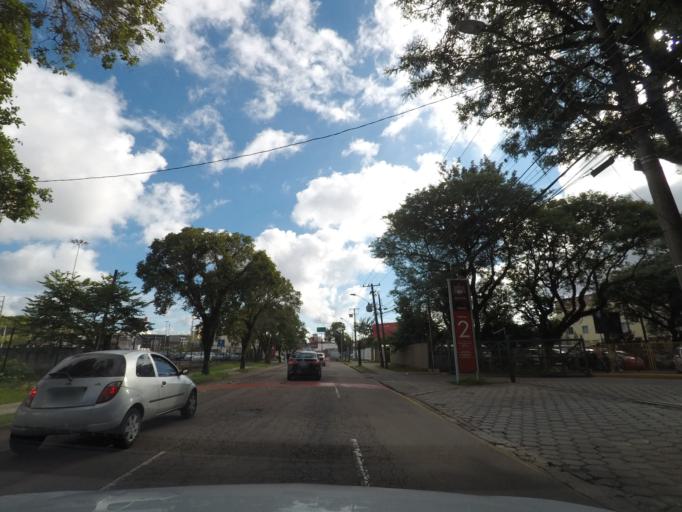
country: BR
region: Parana
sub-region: Curitiba
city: Curitiba
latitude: -25.4491
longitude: -49.2531
